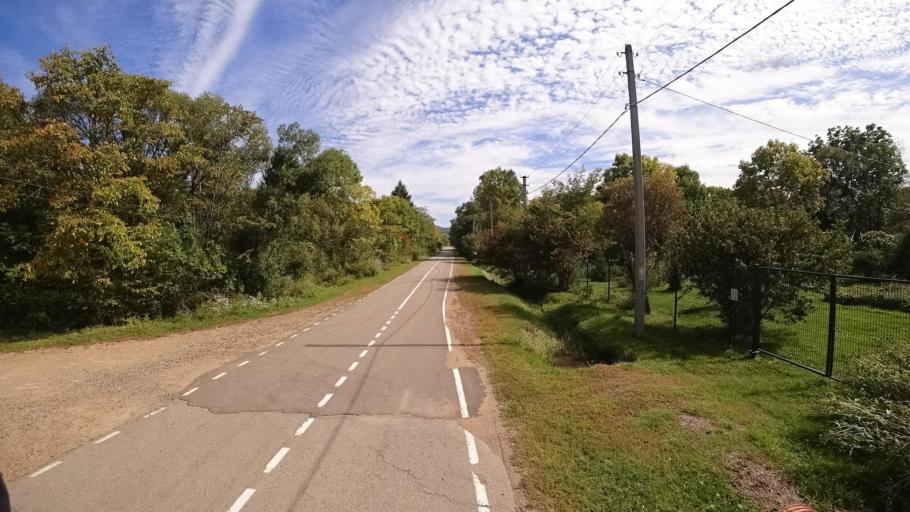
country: RU
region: Primorskiy
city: Yakovlevka
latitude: 44.3963
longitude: 133.6029
